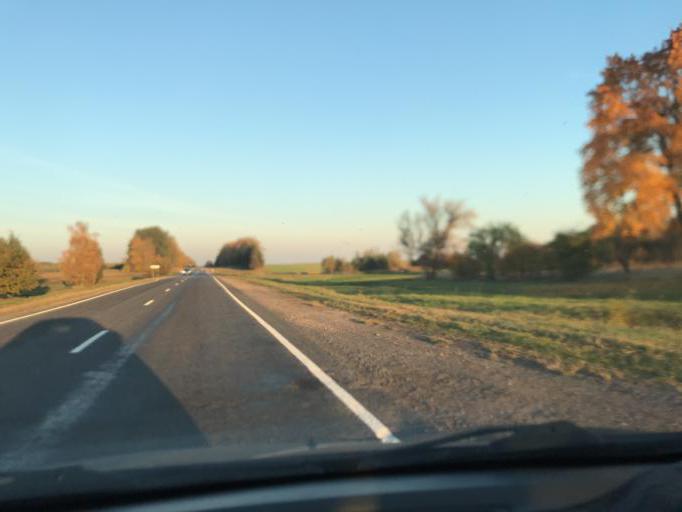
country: BY
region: Minsk
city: Staryya Darohi
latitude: 53.0602
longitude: 28.4811
